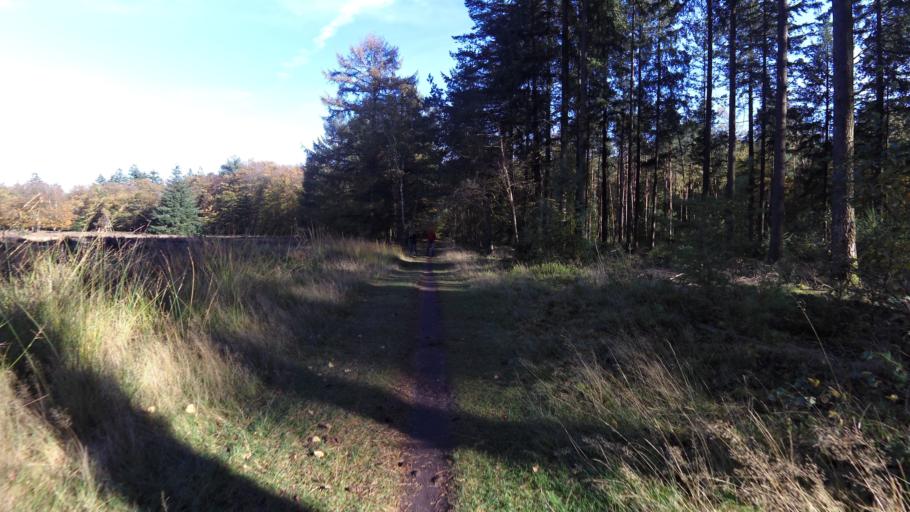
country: NL
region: Gelderland
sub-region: Gemeente Epe
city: Epe
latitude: 52.3764
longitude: 5.9525
